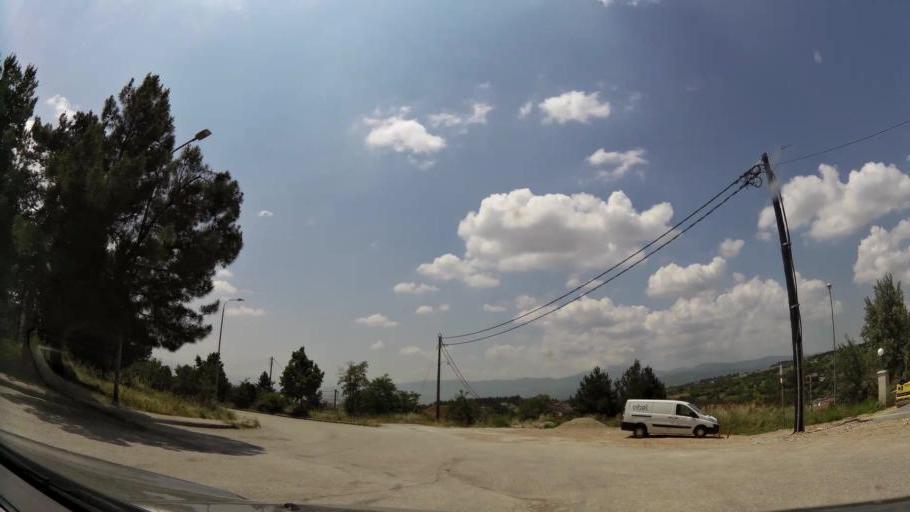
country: GR
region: West Macedonia
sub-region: Nomos Kozanis
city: Kozani
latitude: 40.3021
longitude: 21.7818
